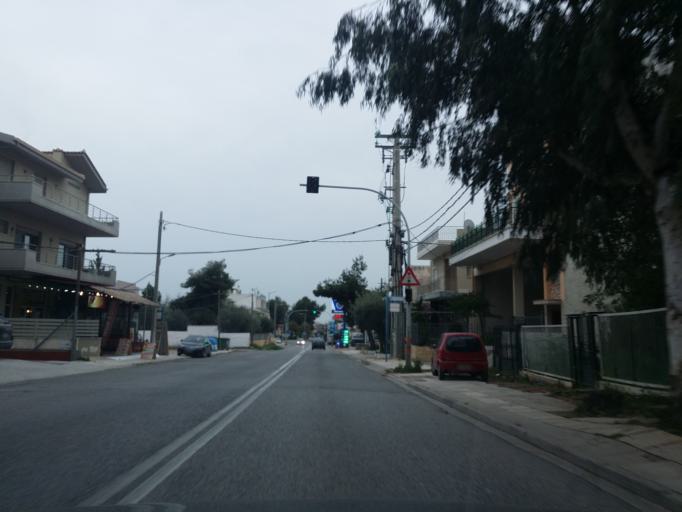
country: GR
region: Attica
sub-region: Nomarchia Dytikis Attikis
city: Mandra
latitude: 38.0804
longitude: 23.4936
